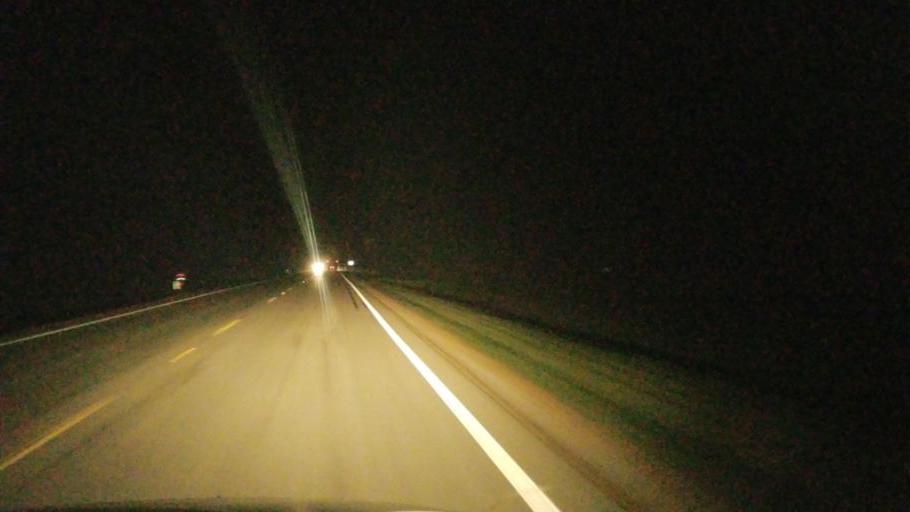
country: US
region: Ohio
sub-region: Highland County
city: Leesburg
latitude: 39.3296
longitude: -83.5640
